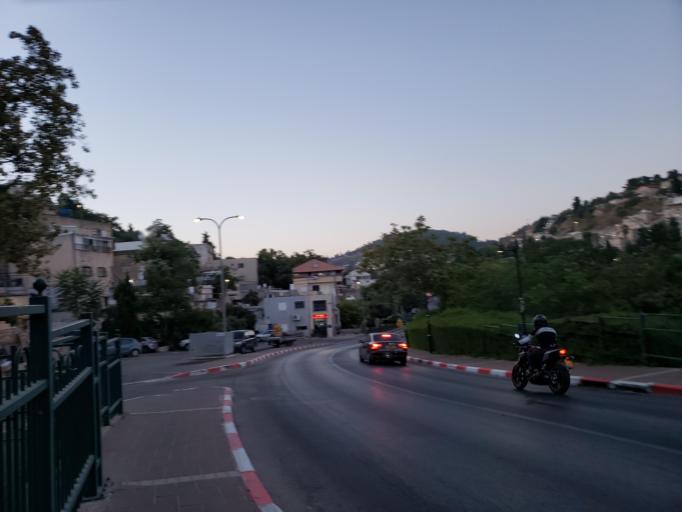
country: IL
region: Northern District
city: Safed
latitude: 32.9664
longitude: 35.4969
